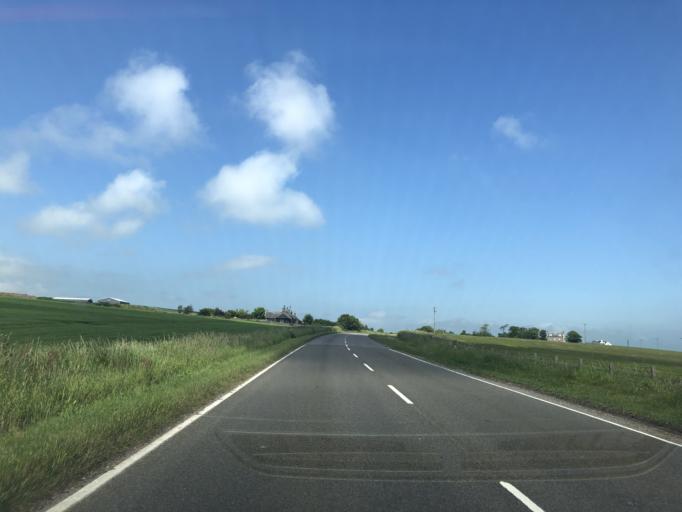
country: GB
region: Scotland
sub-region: Aberdeenshire
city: Stonehaven
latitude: 56.9296
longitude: -2.2072
